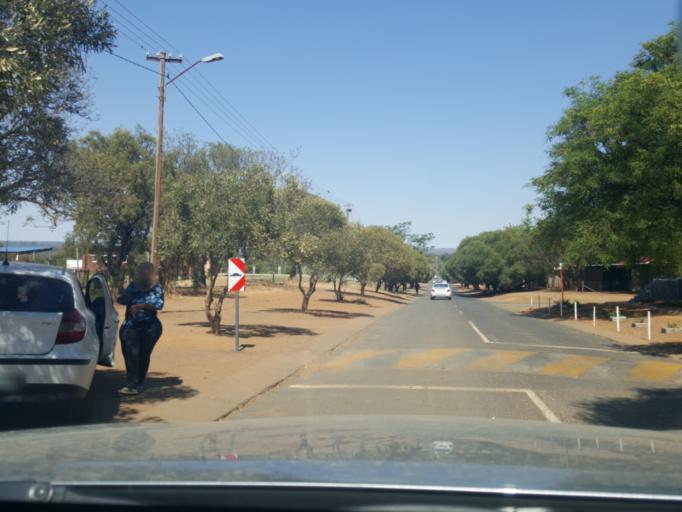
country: ZA
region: North-West
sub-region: Ngaka Modiri Molema District Municipality
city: Zeerust
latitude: -25.5362
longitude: 26.0795
